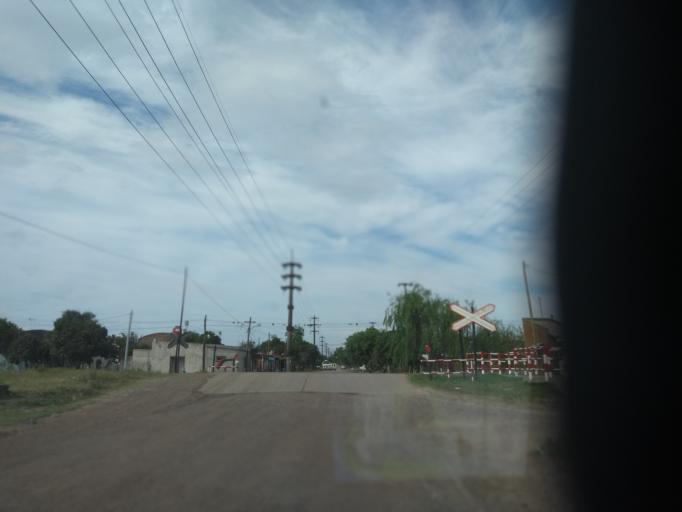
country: AR
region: Chaco
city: Resistencia
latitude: -27.4743
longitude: -58.9695
